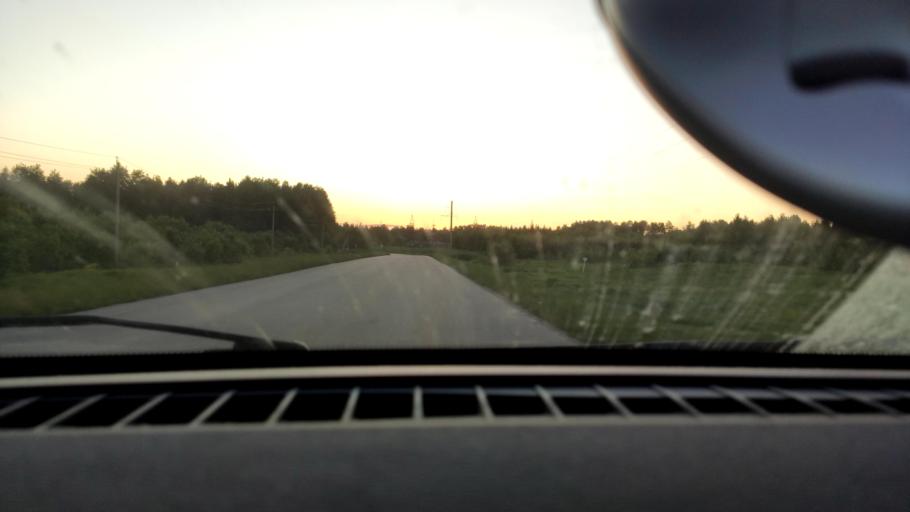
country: RU
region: Perm
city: Polazna
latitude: 58.2082
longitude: 56.5284
